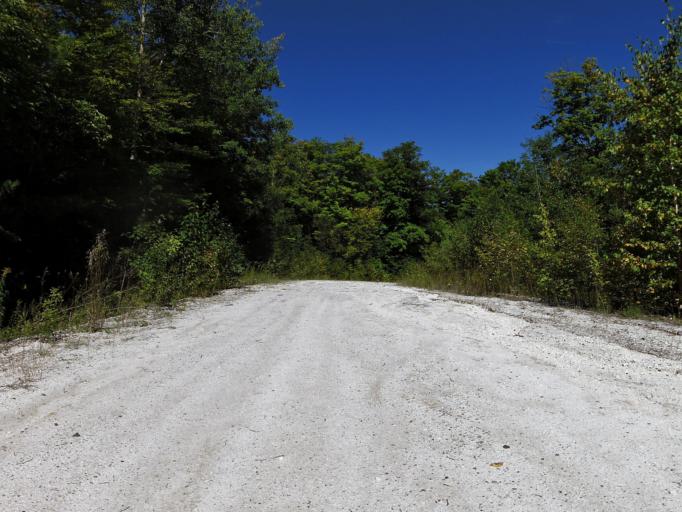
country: CA
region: Ontario
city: Arnprior
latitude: 45.1571
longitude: -76.4954
